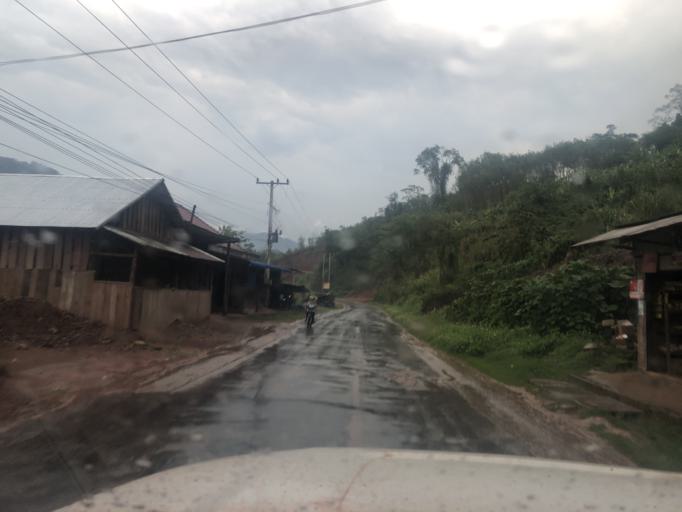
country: LA
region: Phongsali
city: Phongsali
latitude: 21.4027
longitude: 101.9655
